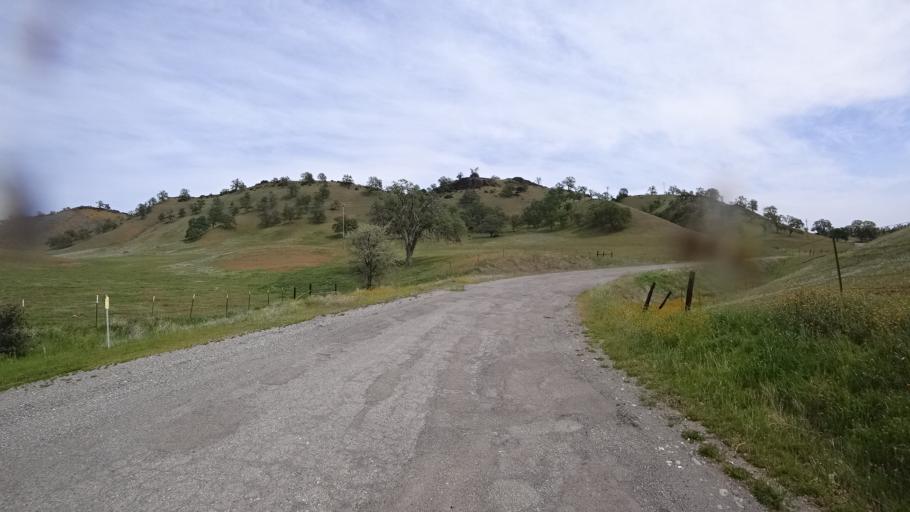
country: US
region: California
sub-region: Glenn County
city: Willows
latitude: 39.6160
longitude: -122.5861
